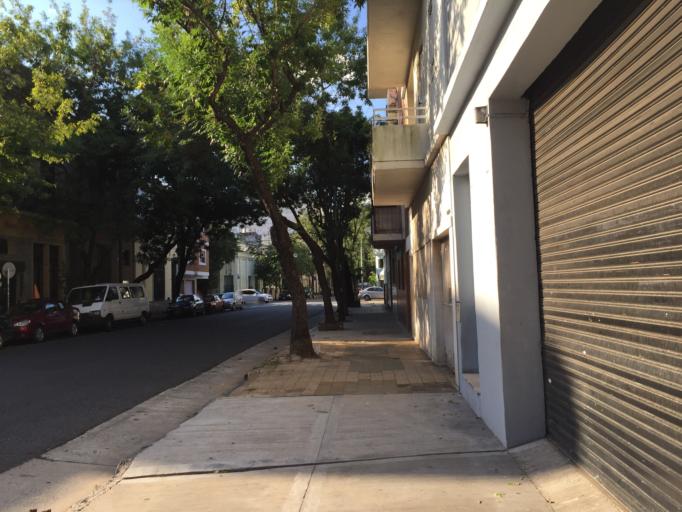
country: AR
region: Buenos Aires F.D.
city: Buenos Aires
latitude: -34.6202
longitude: -58.3986
